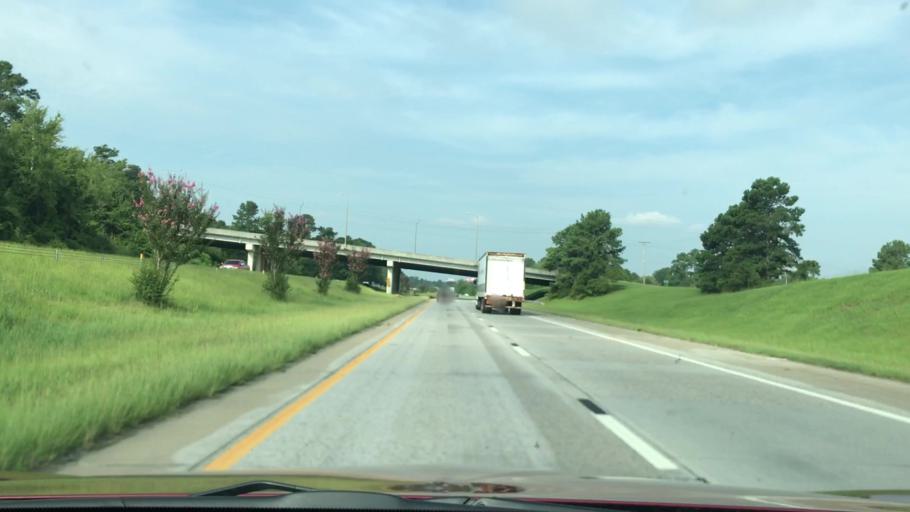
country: US
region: South Carolina
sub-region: Aiken County
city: North Augusta
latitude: 33.5408
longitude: -81.9902
